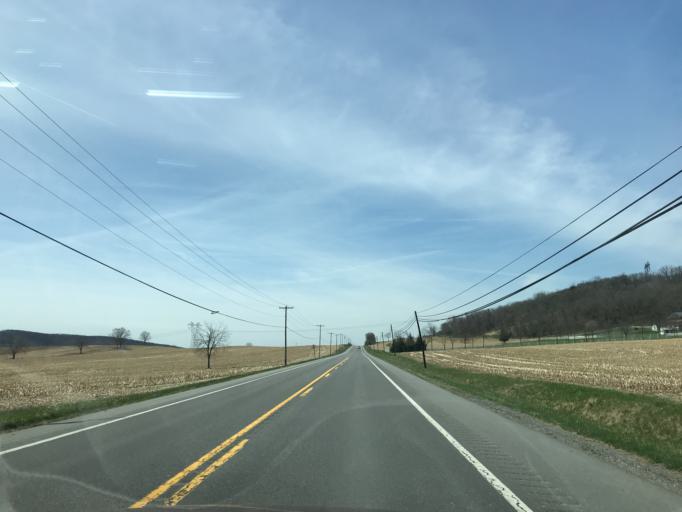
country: US
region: Pennsylvania
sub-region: Snyder County
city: Selinsgrove
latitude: 40.8064
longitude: -76.9262
